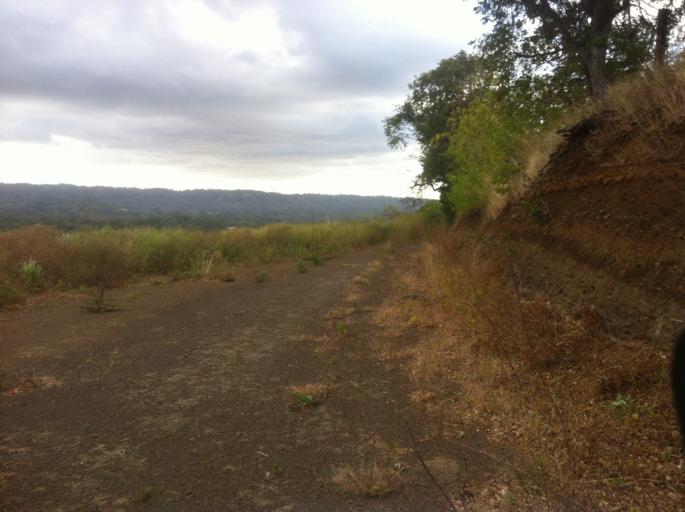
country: NI
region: Managua
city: Ciudad Sandino
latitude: 12.0853
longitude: -86.3259
